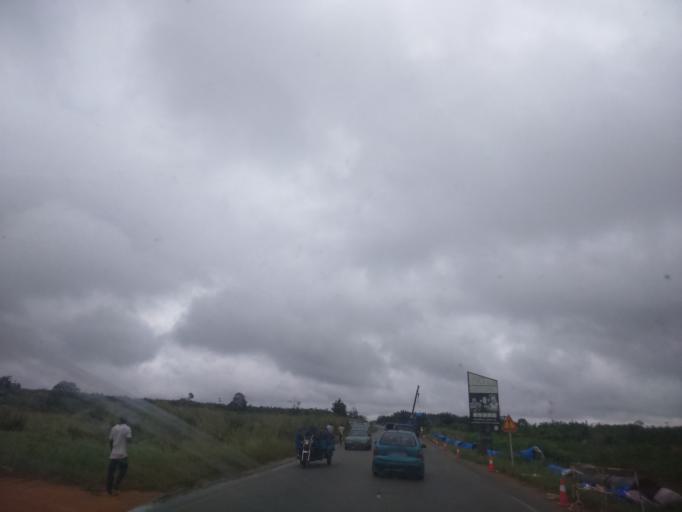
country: CI
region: Sud-Comoe
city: Bonoua
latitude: 5.2760
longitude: -3.5685
